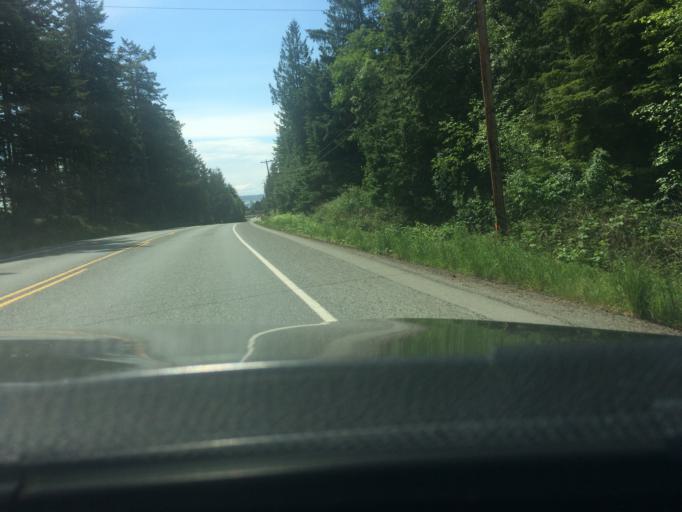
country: US
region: Washington
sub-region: Island County
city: Ault Field
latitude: 48.4291
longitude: -122.6642
